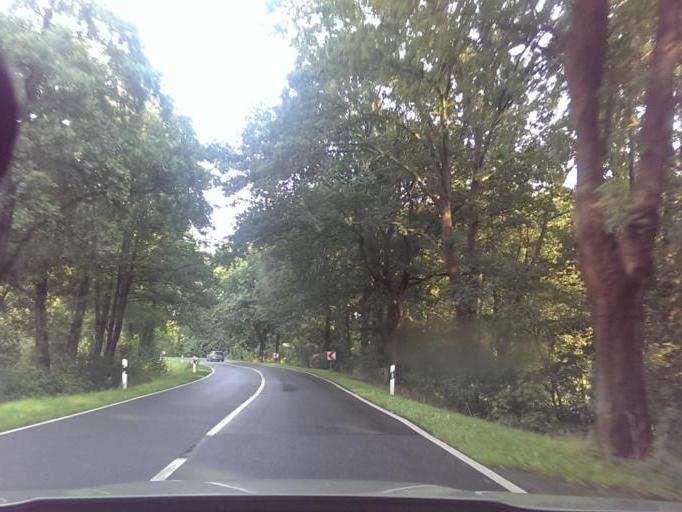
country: DE
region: Lower Saxony
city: Osterholz-Scharmbeck
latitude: 53.1819
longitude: 8.8232
